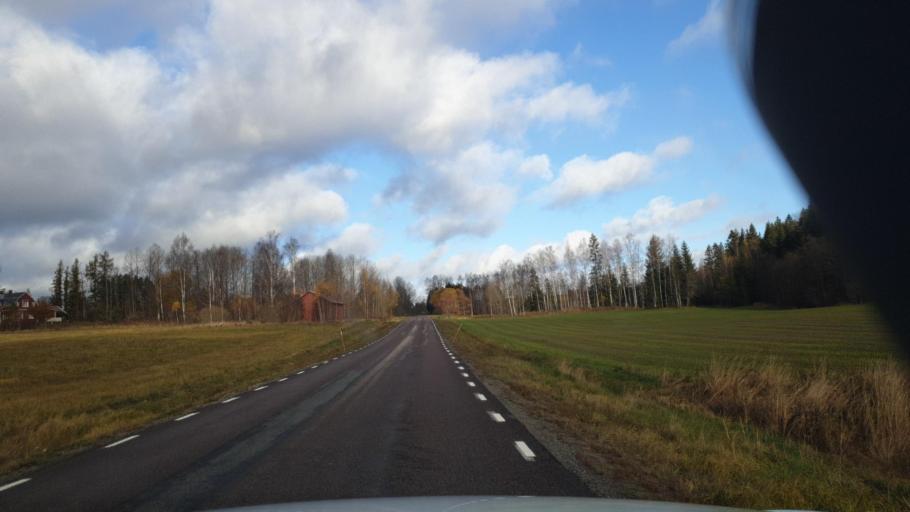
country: SE
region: Vaermland
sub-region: Grums Kommun
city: Slottsbron
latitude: 59.4611
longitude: 12.8769
